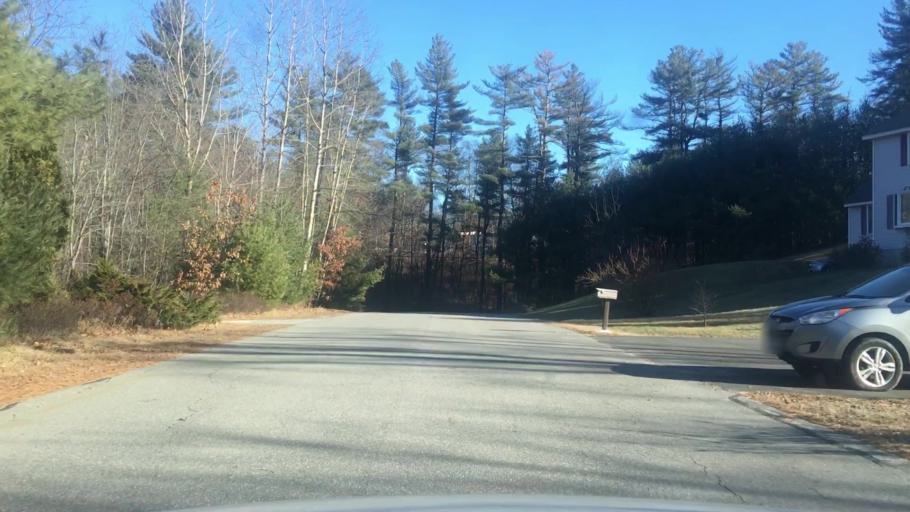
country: US
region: New Hampshire
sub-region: Rockingham County
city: Londonderry
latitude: 42.8898
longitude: -71.4107
